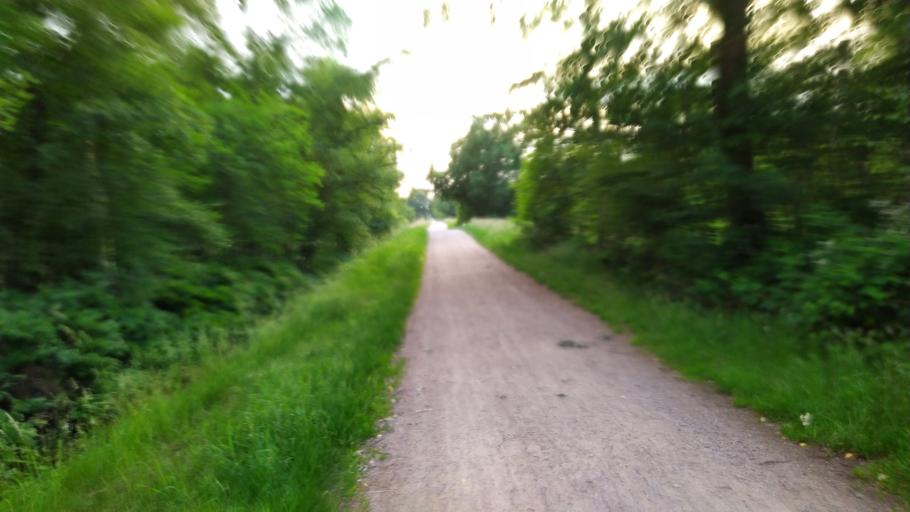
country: DE
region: Lower Saxony
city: Buxtehude
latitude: 53.4789
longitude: 9.6698
